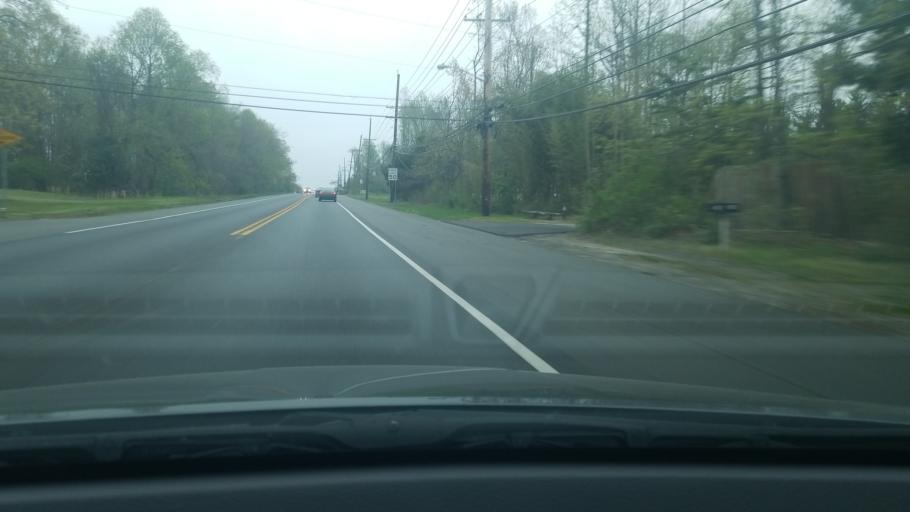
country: US
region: New Jersey
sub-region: Burlington County
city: Medford Lakes
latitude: 39.9045
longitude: -74.8122
